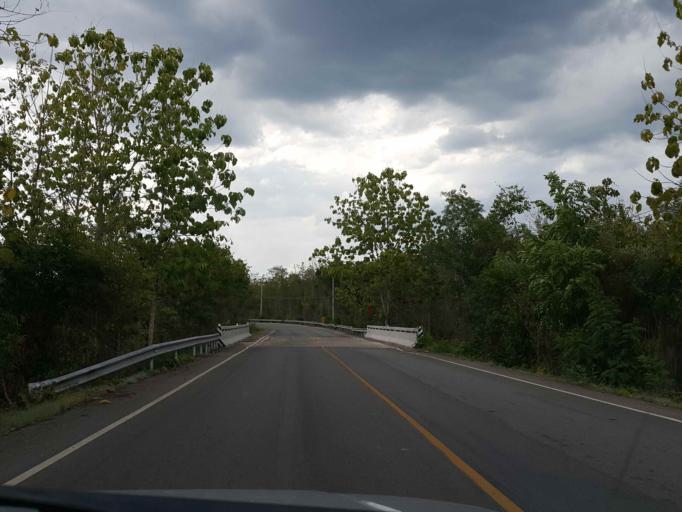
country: TH
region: Sukhothai
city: Thung Saliam
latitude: 17.3630
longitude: 99.4121
